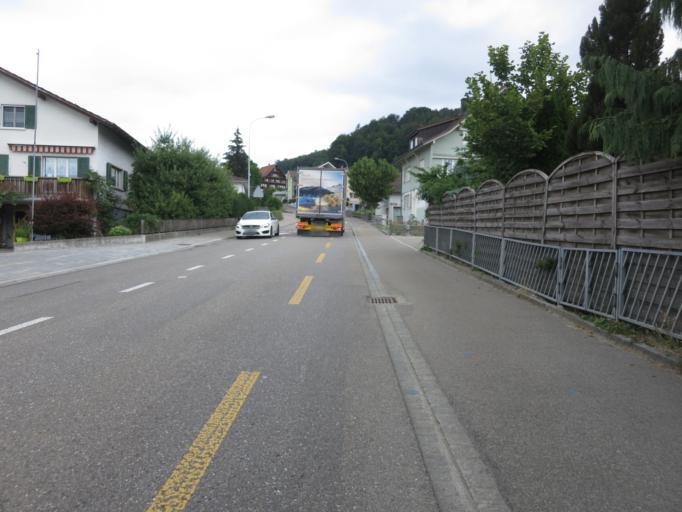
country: CH
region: Saint Gallen
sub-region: Wahlkreis Toggenburg
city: Lutisburg
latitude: 47.3961
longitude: 9.0822
